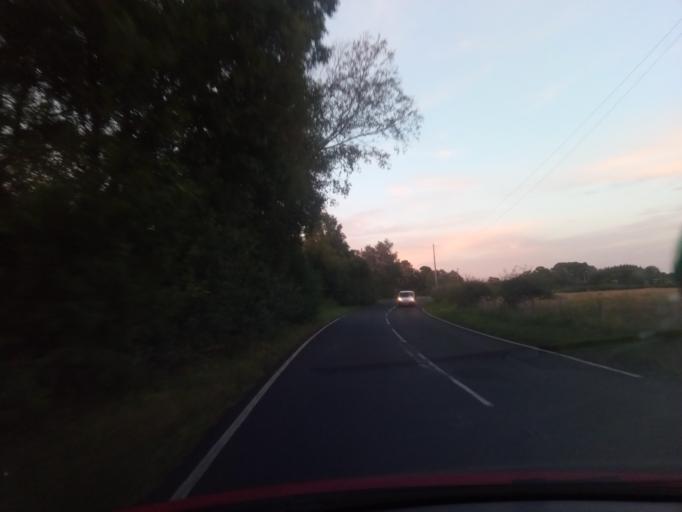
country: GB
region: England
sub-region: Northumberland
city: Bardon Mill
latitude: 54.9450
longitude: -2.2852
